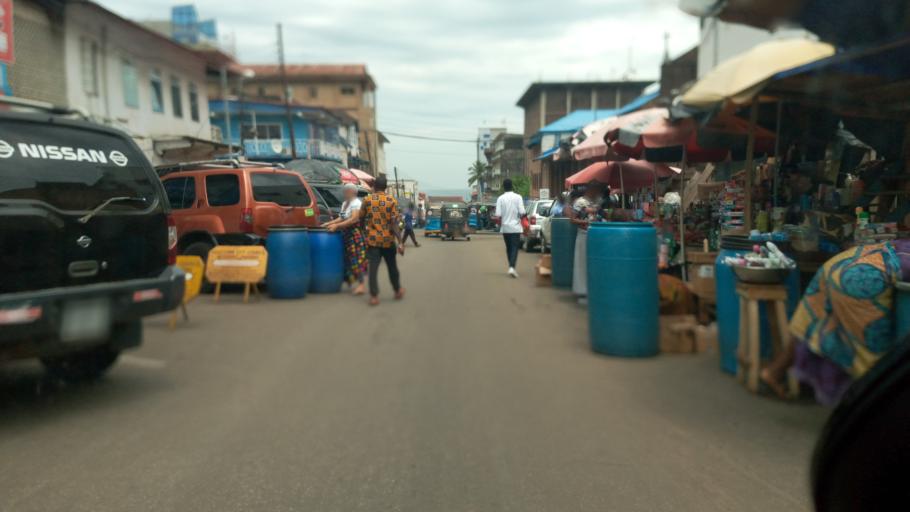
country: SL
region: Western Area
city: Freetown
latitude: 8.4888
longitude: -13.2330
